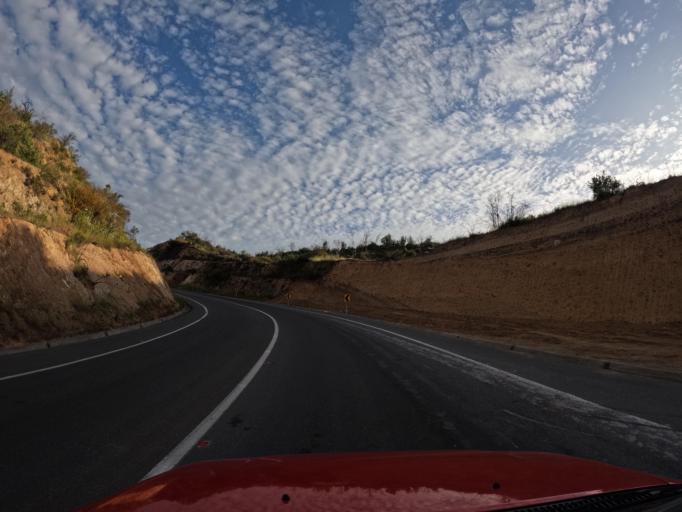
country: CL
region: Valparaiso
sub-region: San Antonio Province
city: San Antonio
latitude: -34.0420
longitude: -71.5932
